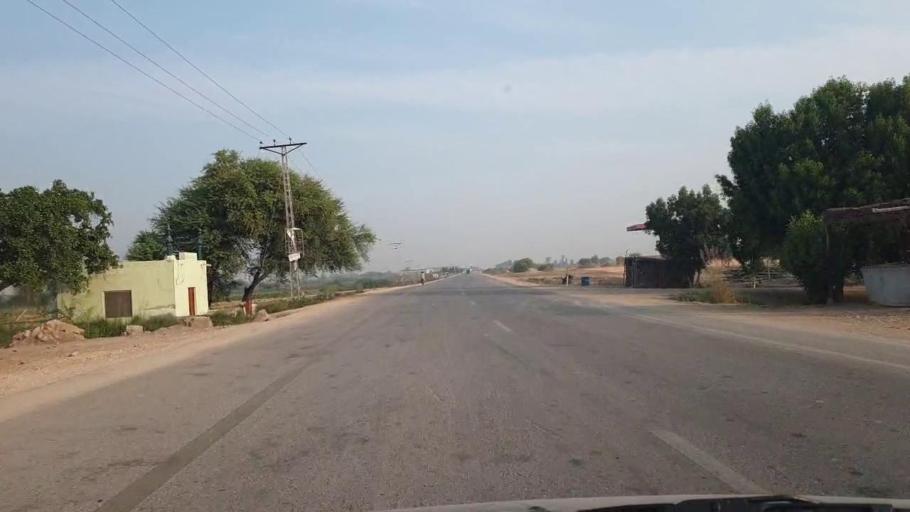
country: PK
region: Sindh
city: Badin
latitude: 24.6884
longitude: 68.8237
